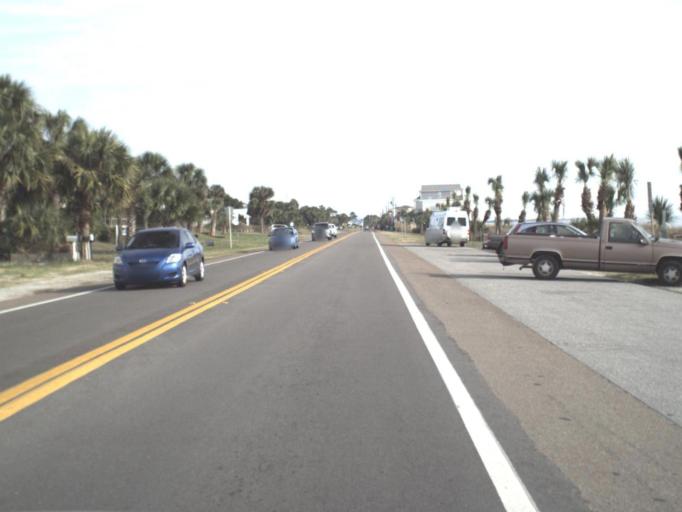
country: US
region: Florida
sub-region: Bay County
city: Mexico Beach
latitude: 29.9250
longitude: -85.3884
